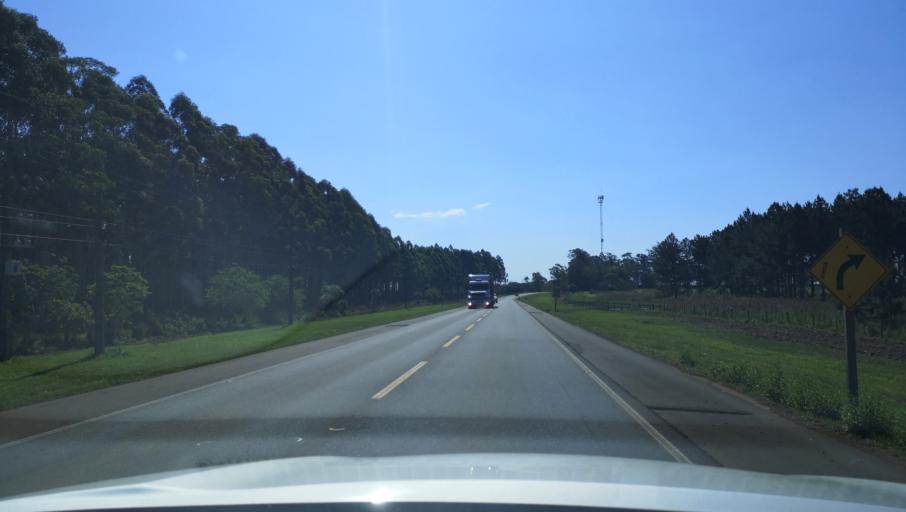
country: PY
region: Itapua
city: General Delgado
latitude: -27.0613
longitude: -56.6265
